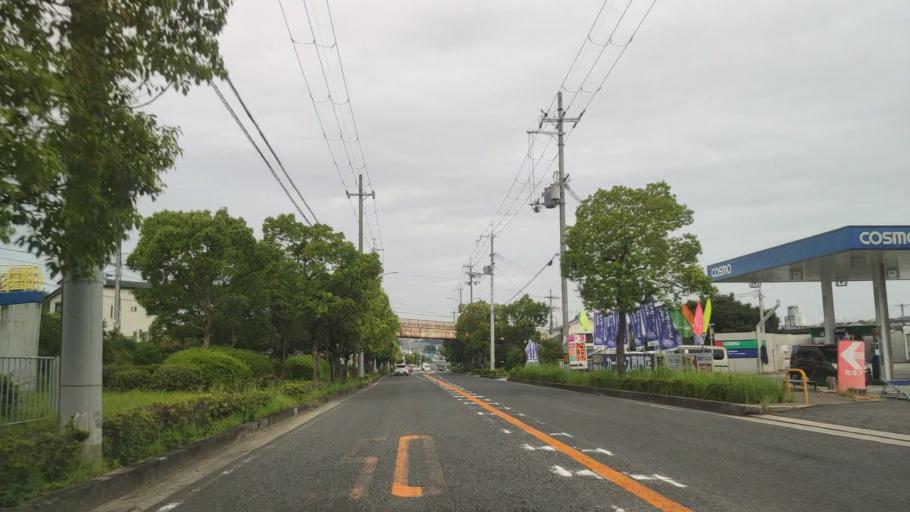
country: JP
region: Osaka
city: Tondabayashicho
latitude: 34.4266
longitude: 135.5712
